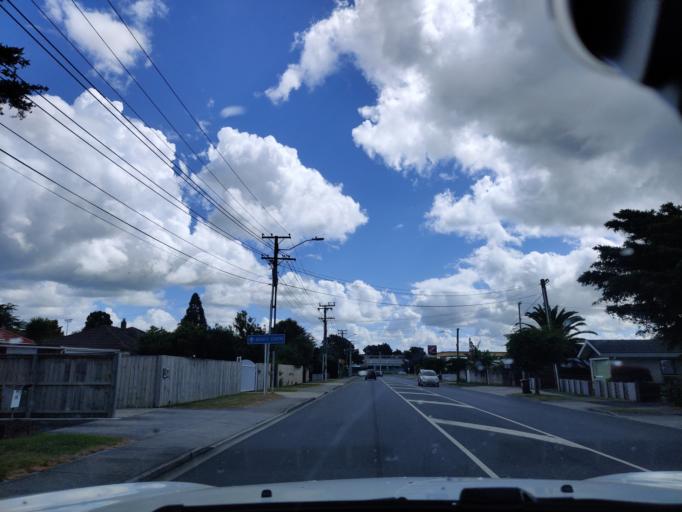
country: NZ
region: Auckland
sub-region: Auckland
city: Papakura
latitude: -37.0612
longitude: 174.9496
